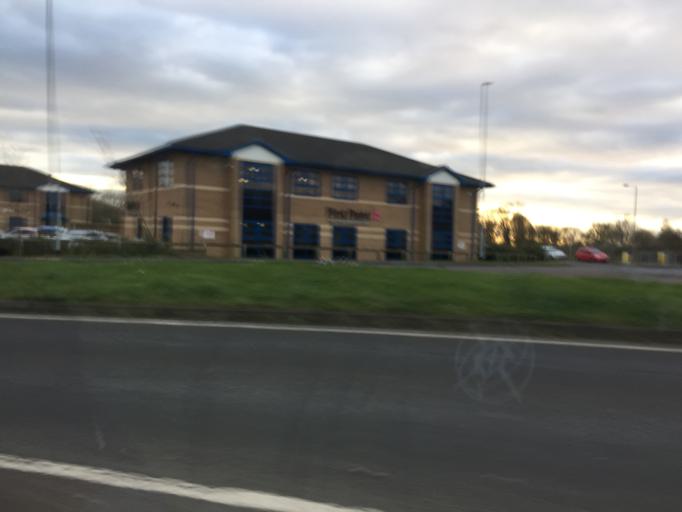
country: GB
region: England
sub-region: Northamptonshire
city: Northampton
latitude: 52.2739
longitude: -0.8645
